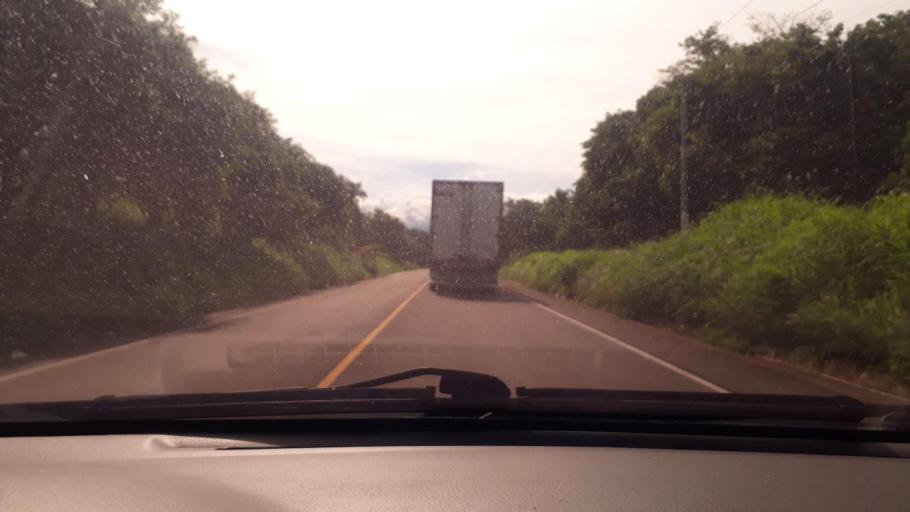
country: SV
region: Ahuachapan
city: San Francisco Menendez
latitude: 13.8791
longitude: -90.1173
